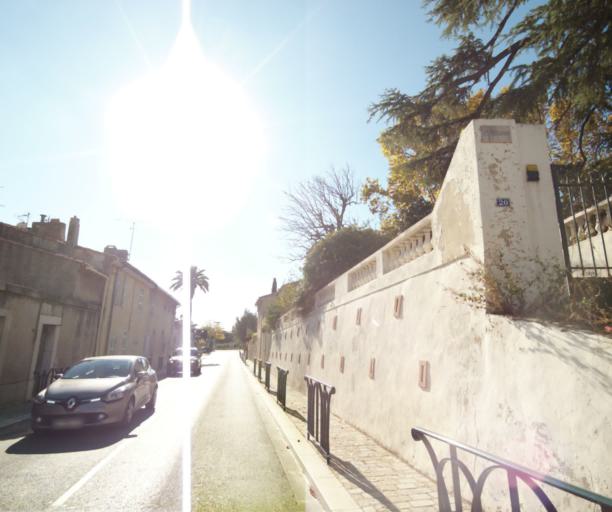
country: FR
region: Provence-Alpes-Cote d'Azur
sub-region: Departement des Bouches-du-Rhone
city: Ceyreste
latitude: 43.2127
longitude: 5.6295
